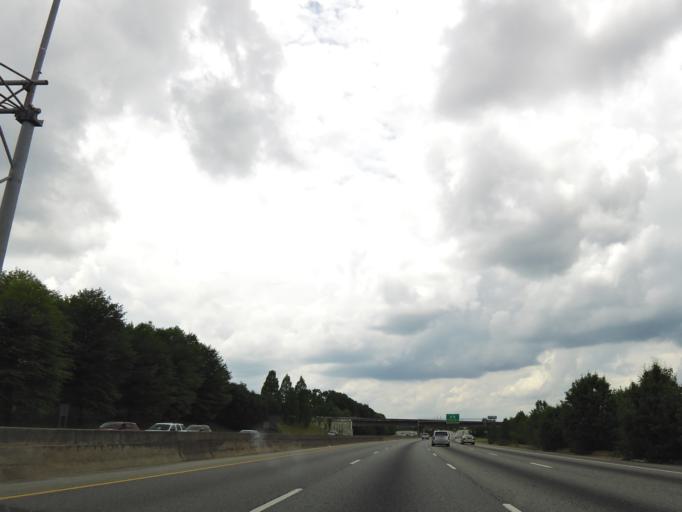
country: US
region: Georgia
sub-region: Fulton County
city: College Park
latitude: 33.6182
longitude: -84.4557
